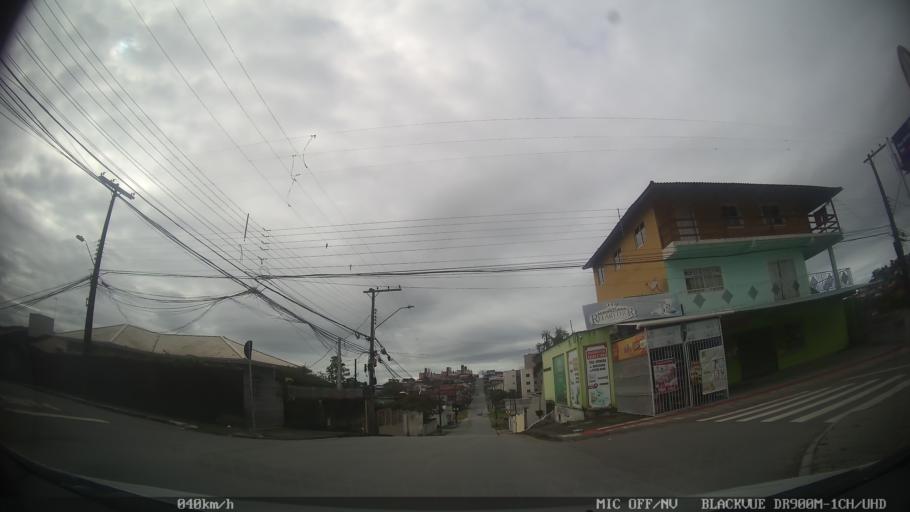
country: BR
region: Santa Catarina
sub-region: Biguacu
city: Biguacu
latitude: -27.5447
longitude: -48.6444
